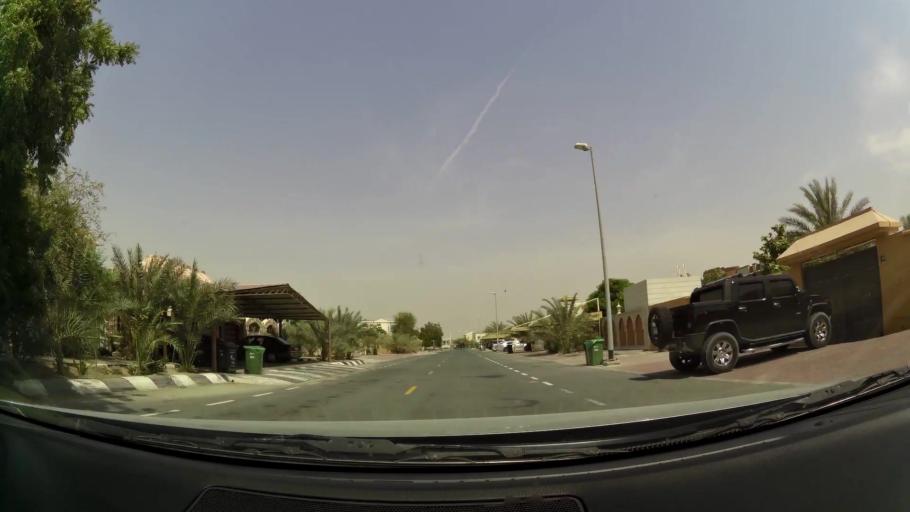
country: AE
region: Ash Shariqah
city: Sharjah
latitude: 25.2428
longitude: 55.4302
